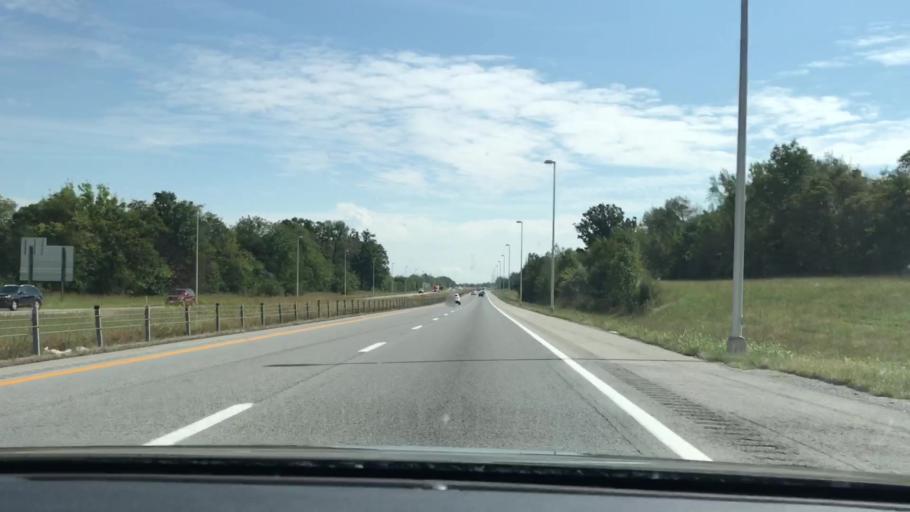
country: US
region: Kentucky
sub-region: Christian County
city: Fort Campbell North
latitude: 36.7415
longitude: -87.5071
